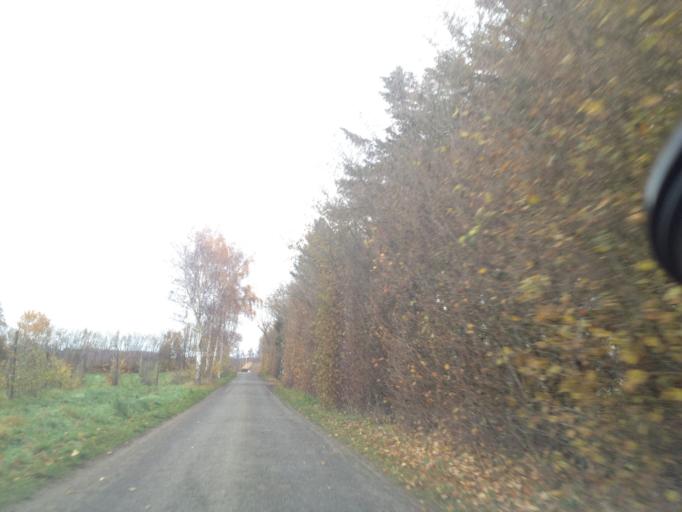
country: DK
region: South Denmark
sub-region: Assens Kommune
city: Vissenbjerg
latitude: 55.4115
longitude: 10.1531
